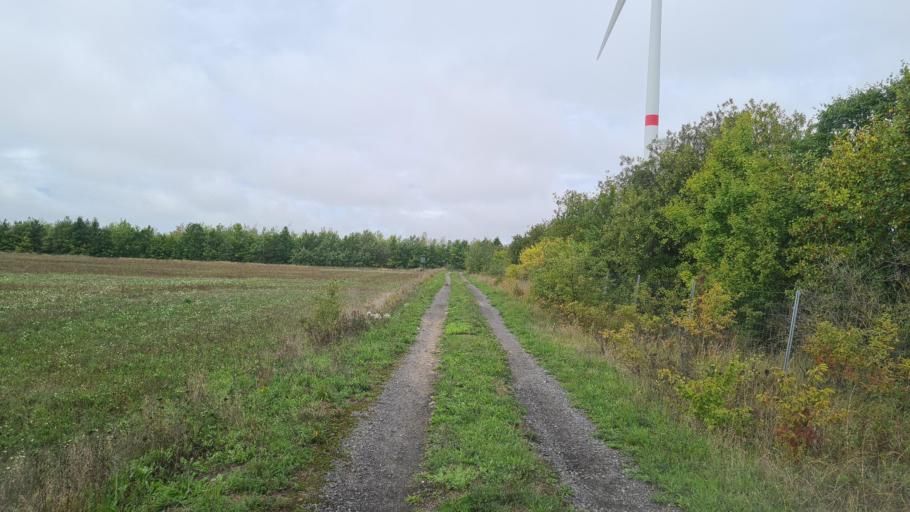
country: DE
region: Brandenburg
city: Sallgast
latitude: 51.5576
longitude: 13.8252
